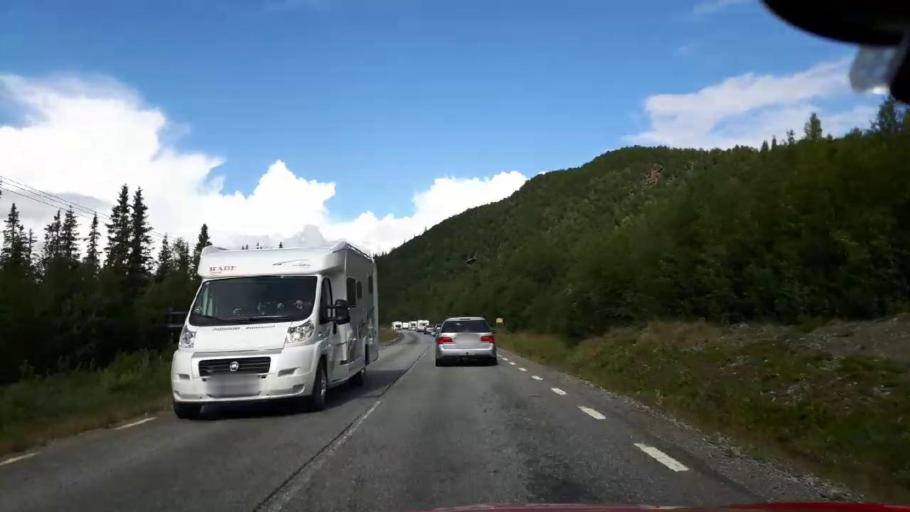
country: SE
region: Vaesterbotten
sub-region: Vilhelmina Kommun
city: Sjoberg
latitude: 65.0352
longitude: 15.1365
